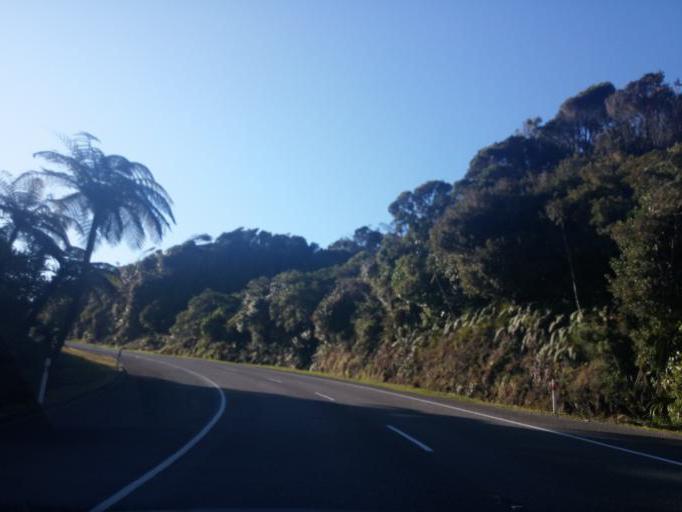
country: NZ
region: West Coast
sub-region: Grey District
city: Greymouth
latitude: -42.1000
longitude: 171.3421
